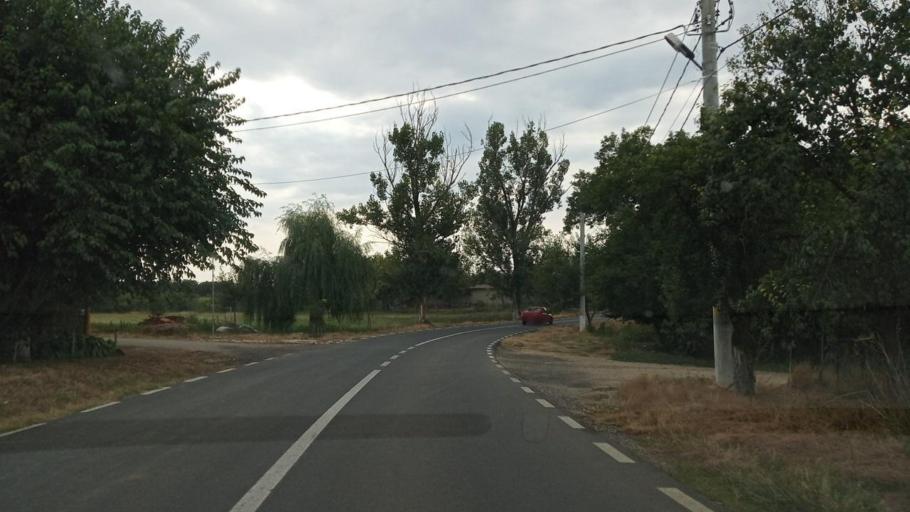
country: RO
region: Giurgiu
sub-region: Comuna Gostinari
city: Gostinari
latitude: 44.1729
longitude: 26.2420
